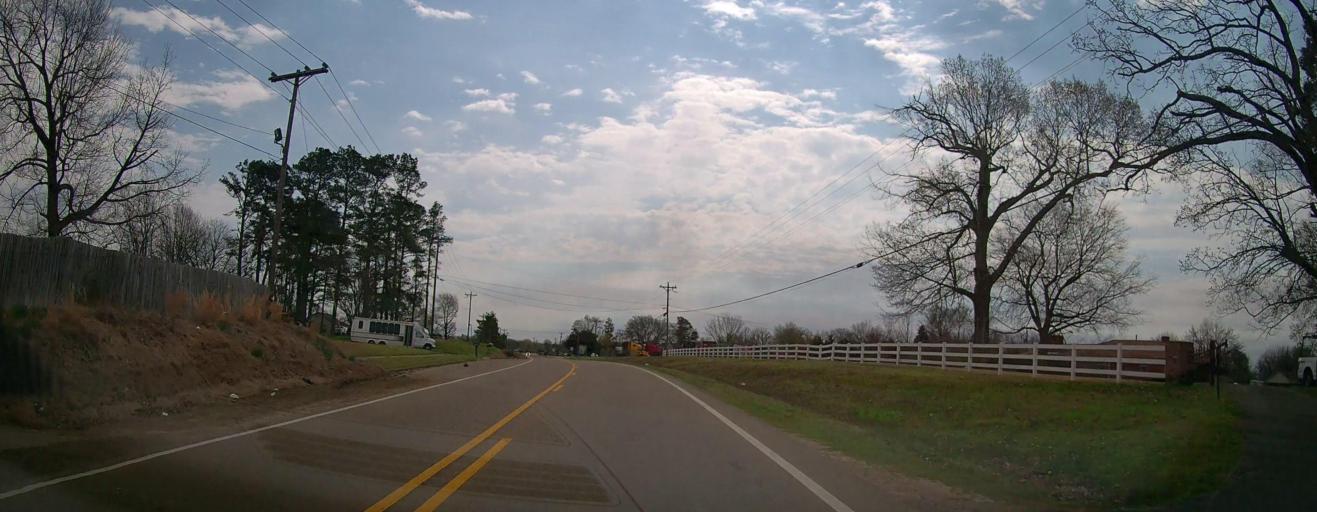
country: US
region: Mississippi
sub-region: De Soto County
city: Olive Branch
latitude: 34.9811
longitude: -89.8563
